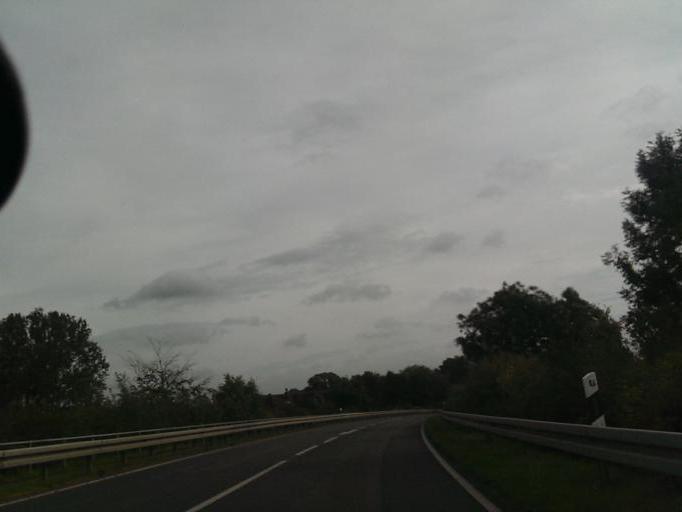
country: DE
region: Lower Saxony
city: Garbsen
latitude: 52.4619
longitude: 9.5397
